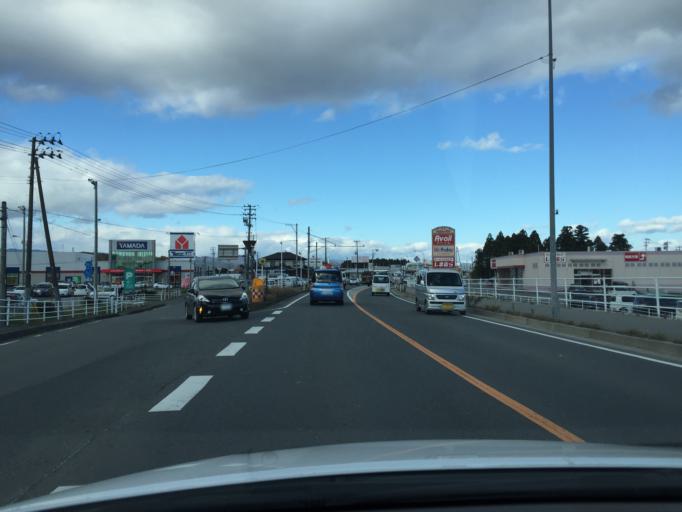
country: JP
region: Fukushima
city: Namie
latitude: 37.6242
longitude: 140.9929
